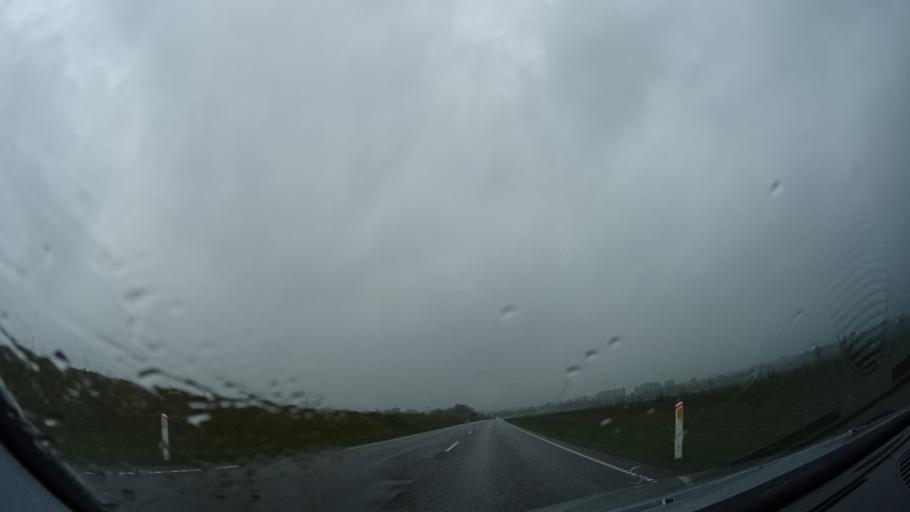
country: DK
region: Zealand
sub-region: Holbaek Kommune
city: Holbaek
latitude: 55.7160
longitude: 11.6254
